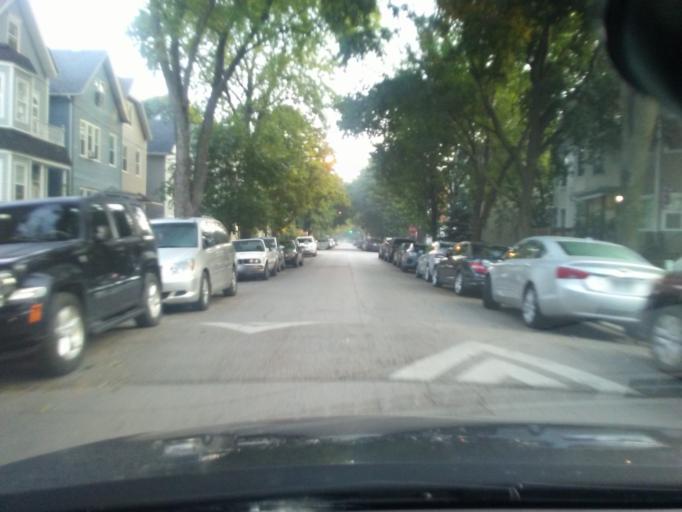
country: US
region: Illinois
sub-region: Cook County
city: Lincolnwood
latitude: 41.9371
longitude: -87.6831
